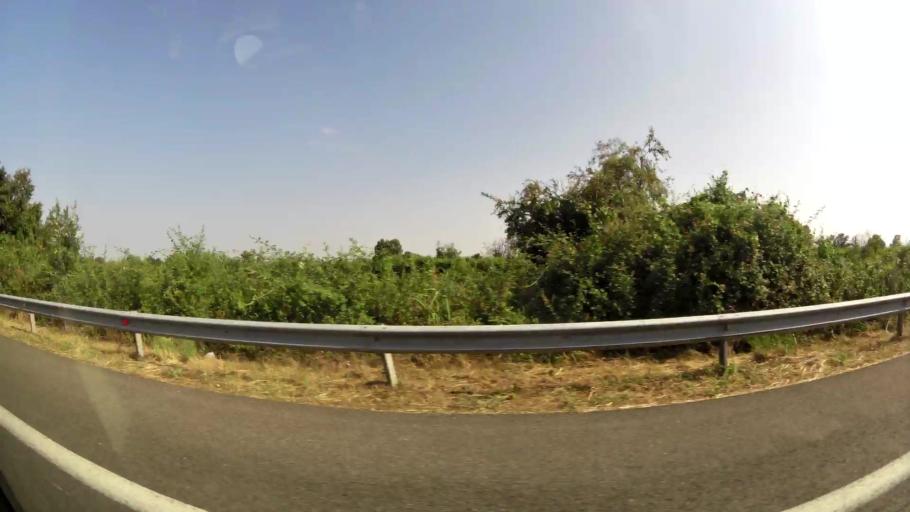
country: GR
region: Central Macedonia
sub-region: Nomos Imathias
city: Loutros
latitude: 40.5875
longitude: 22.4373
